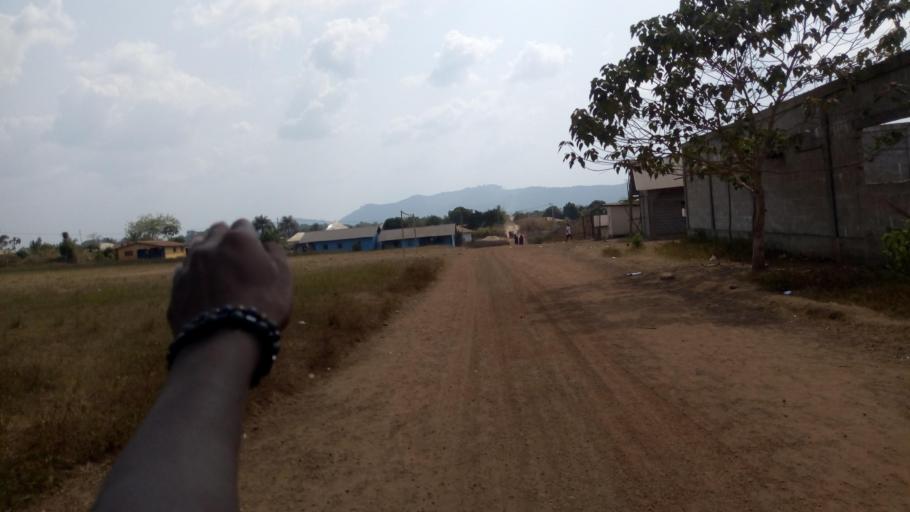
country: SL
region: Southern Province
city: Mogbwemo
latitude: 7.7793
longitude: -12.3007
